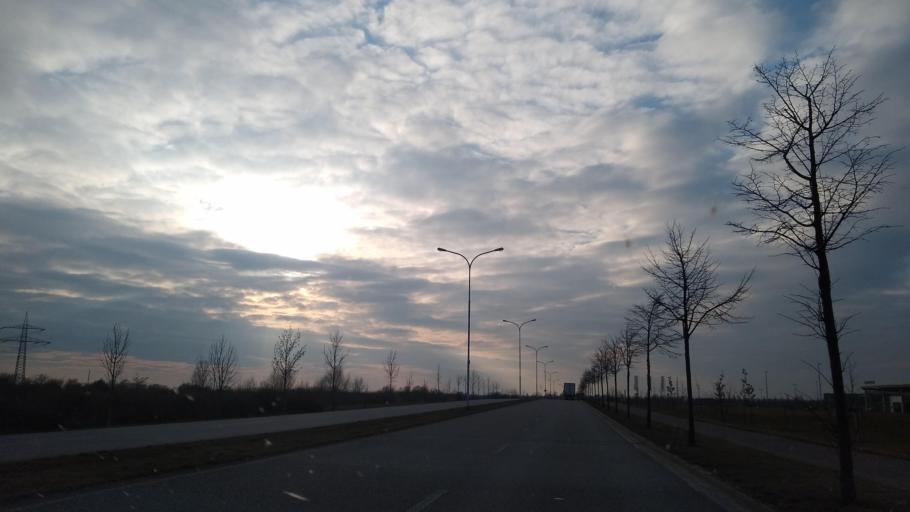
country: DE
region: Saxony-Anhalt
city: Dolbau
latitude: 51.4815
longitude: 12.0813
